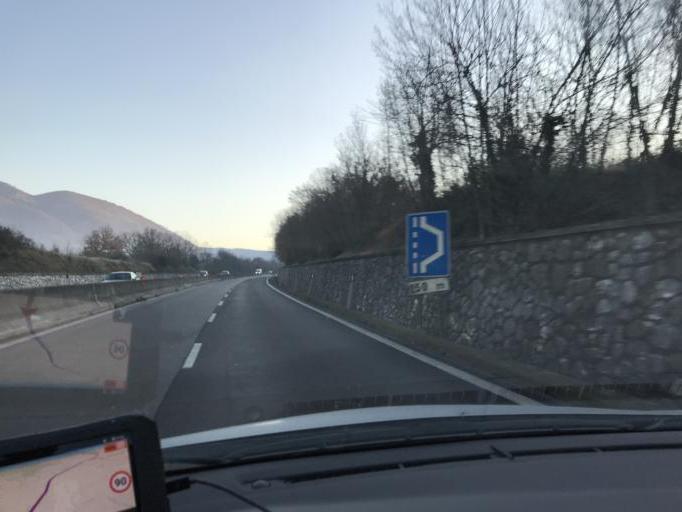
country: IT
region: Umbria
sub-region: Provincia di Terni
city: Terni
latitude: 42.5835
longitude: 12.6433
